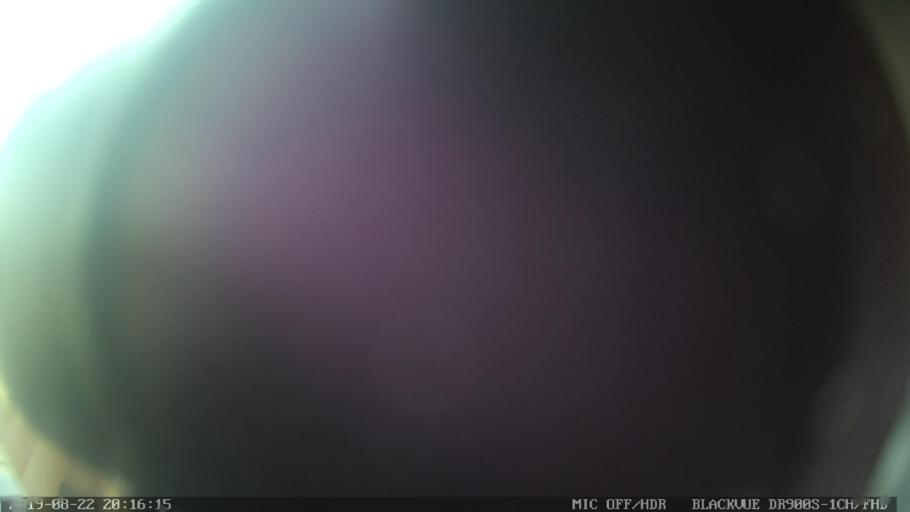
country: PT
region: Guarda
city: Alcains
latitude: 39.9246
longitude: -7.4503
